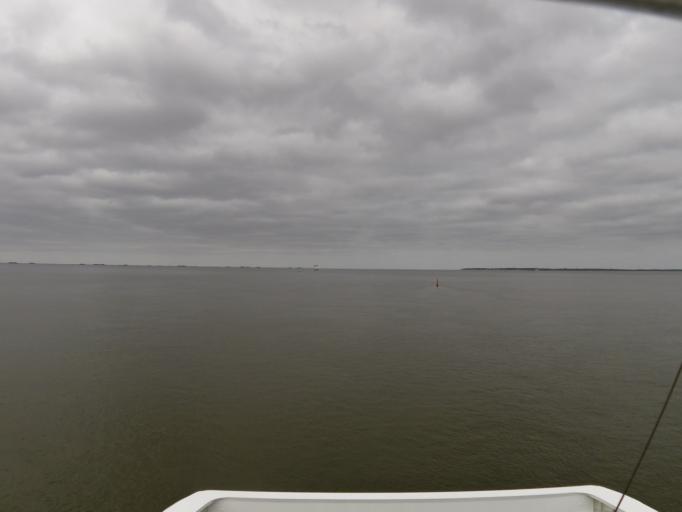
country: DE
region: Schleswig-Holstein
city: Dagebull
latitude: 54.7123
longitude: 8.6572
